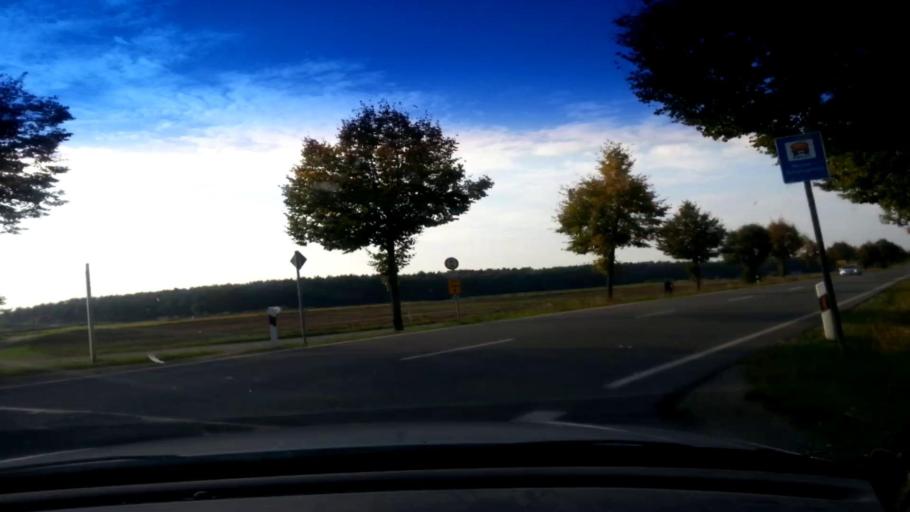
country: DE
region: Bavaria
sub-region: Upper Franconia
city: Hirschaid
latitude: 49.8227
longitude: 10.9849
